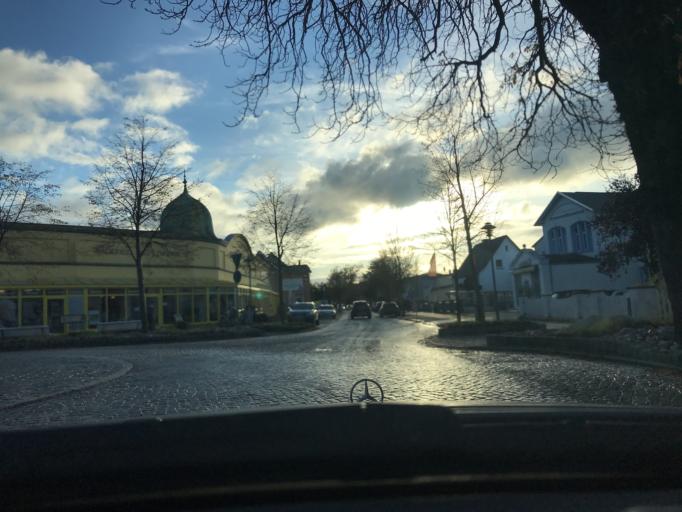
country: DE
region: Mecklenburg-Vorpommern
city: Ostseebad Zinnowitz
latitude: 54.0769
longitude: 13.9093
